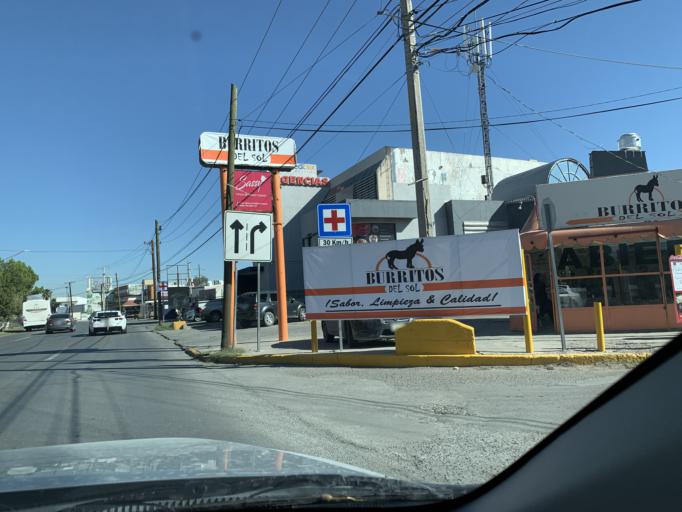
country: MX
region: Chihuahua
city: Ciudad Juarez
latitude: 31.7501
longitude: -106.4263
